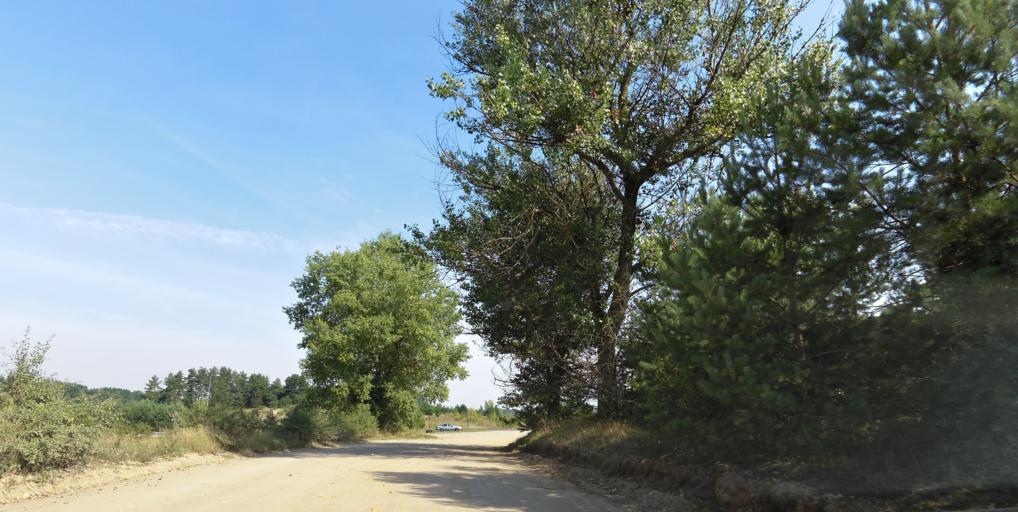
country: LT
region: Vilnius County
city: Pilaite
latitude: 54.7034
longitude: 25.1967
